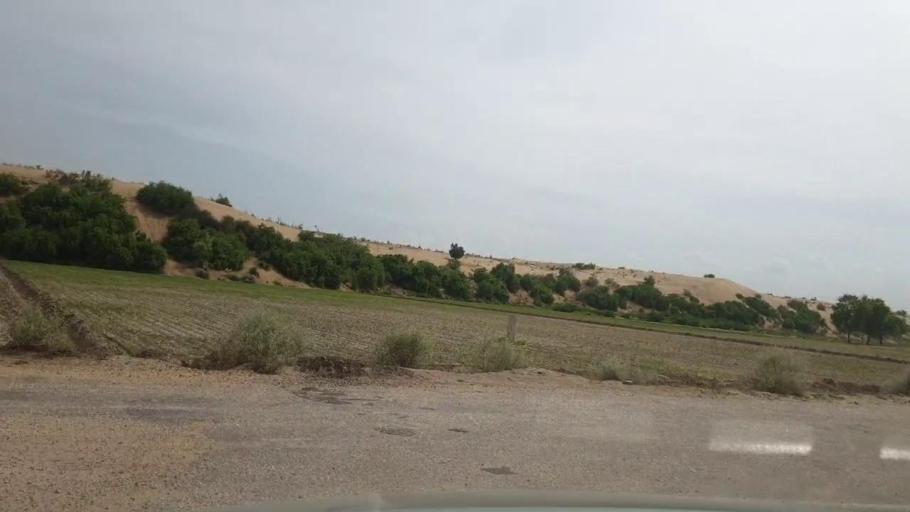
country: PK
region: Sindh
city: Bozdar
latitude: 27.0759
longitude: 69.0135
